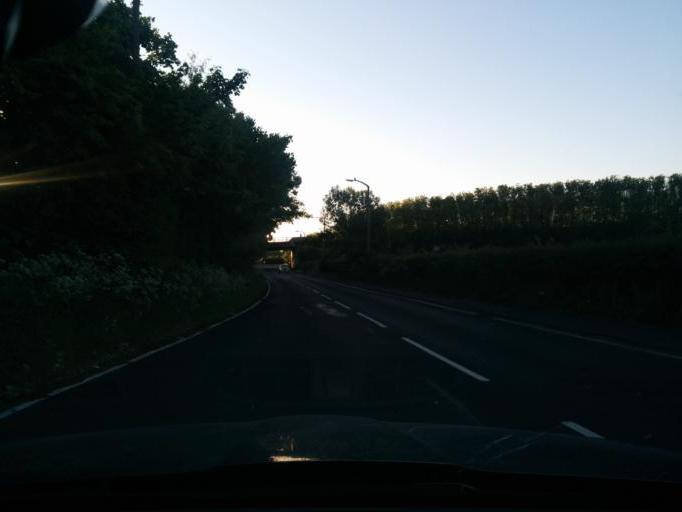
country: GB
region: England
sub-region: Northumberland
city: Cramlington
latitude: 55.1024
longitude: -1.5725
